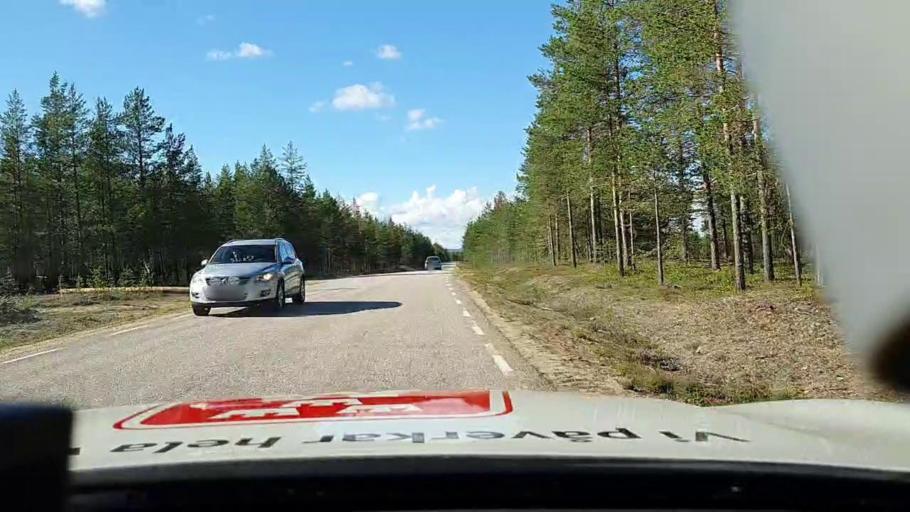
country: SE
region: Norrbotten
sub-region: Overkalix Kommun
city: OEverkalix
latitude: 66.2382
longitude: 22.9315
